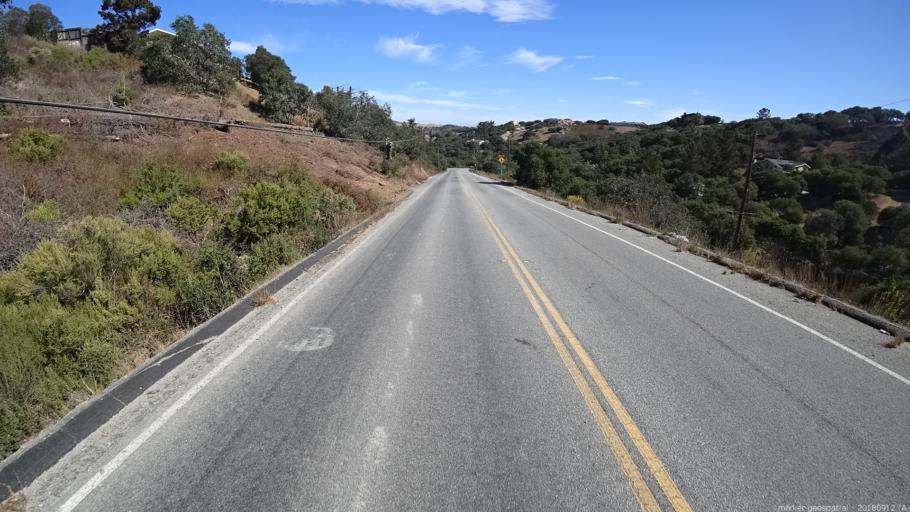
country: US
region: California
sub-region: Monterey County
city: Carmel Valley Village
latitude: 36.5596
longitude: -121.7504
